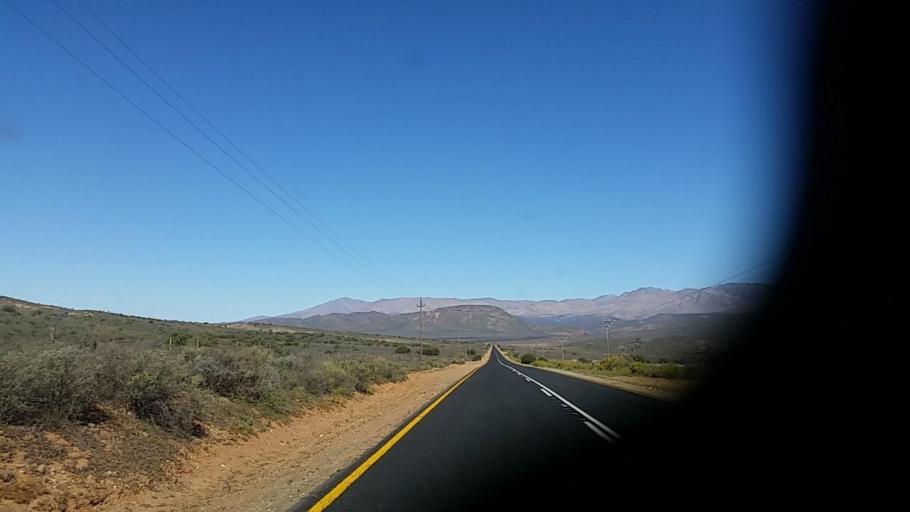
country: ZA
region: Western Cape
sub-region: Eden District Municipality
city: Oudtshoorn
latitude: -33.4855
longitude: 22.6631
